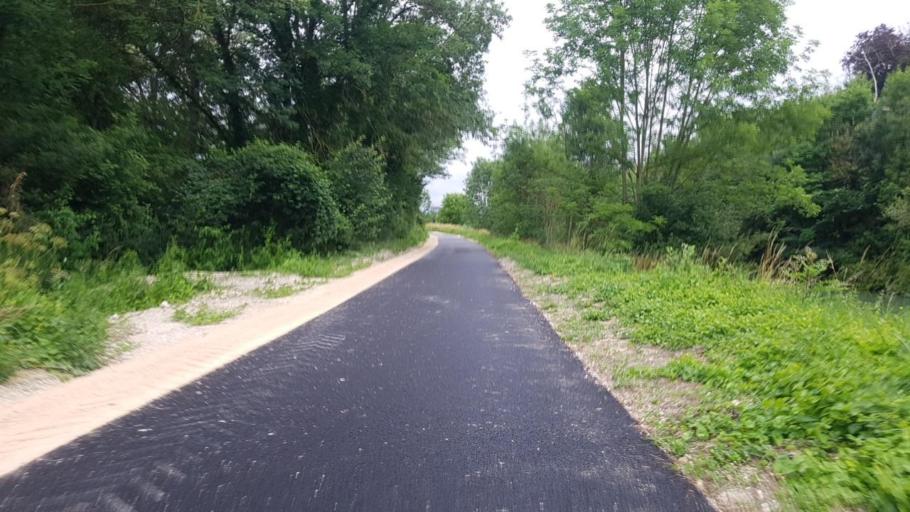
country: FR
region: Champagne-Ardenne
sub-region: Departement de la Marne
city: Sarry
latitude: 48.8500
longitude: 4.4875
